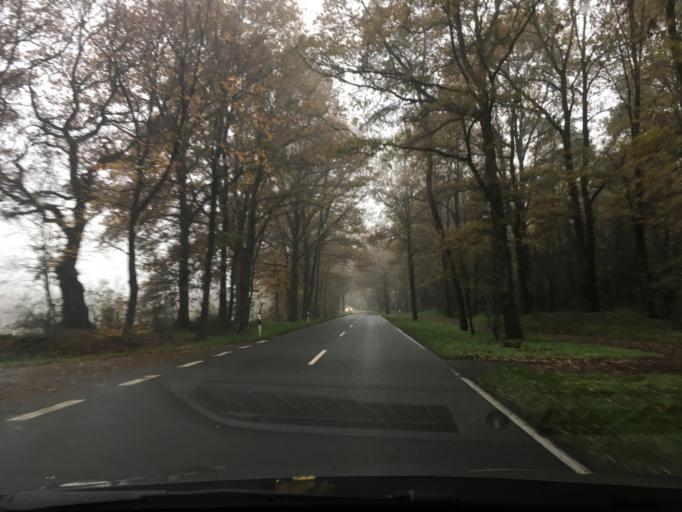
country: DE
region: North Rhine-Westphalia
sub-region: Regierungsbezirk Munster
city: Ahaus
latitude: 52.0988
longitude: 6.9136
